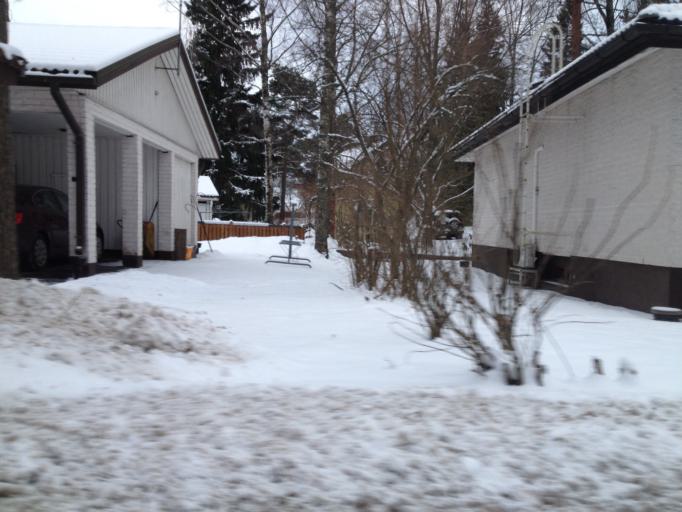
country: FI
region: Uusimaa
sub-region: Helsinki
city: Vantaa
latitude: 60.2221
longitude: 25.1068
